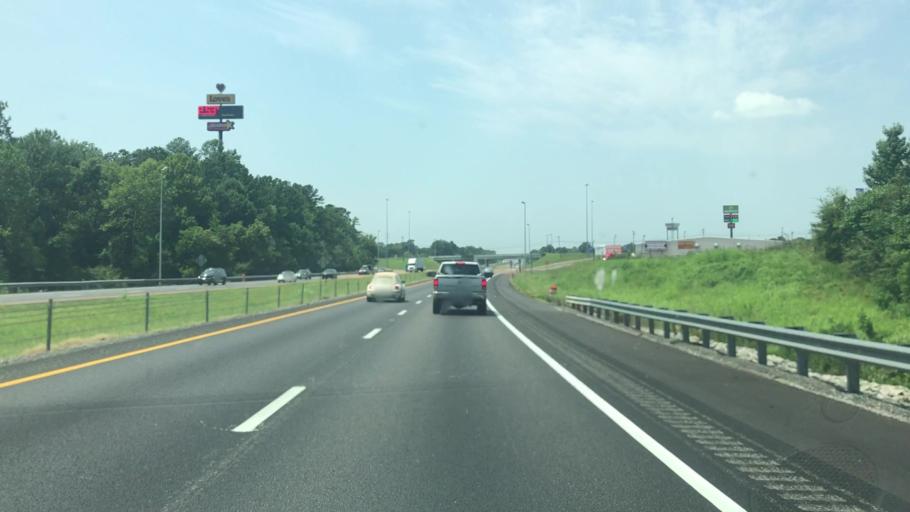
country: US
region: Tennessee
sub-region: Madison County
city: Jackson
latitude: 35.6813
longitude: -88.7369
